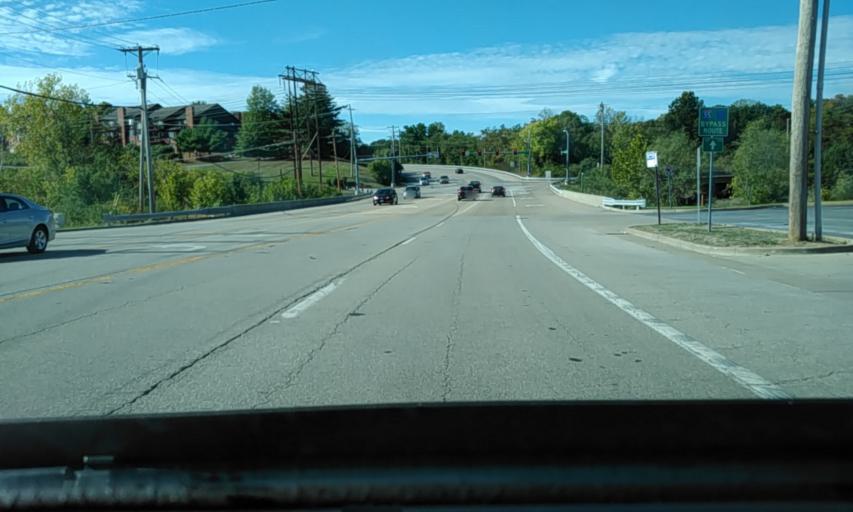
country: US
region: Missouri
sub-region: Saint Louis County
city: Mehlville
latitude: 38.4953
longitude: -90.3437
